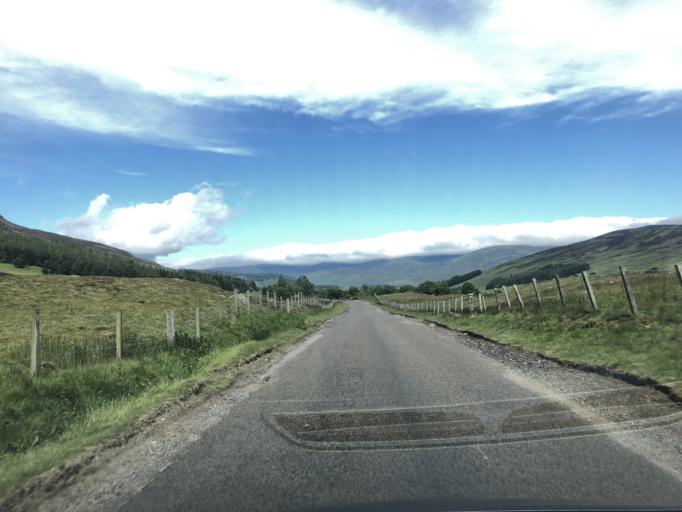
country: GB
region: Scotland
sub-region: Angus
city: Kirriemuir
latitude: 56.7697
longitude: -3.0250
